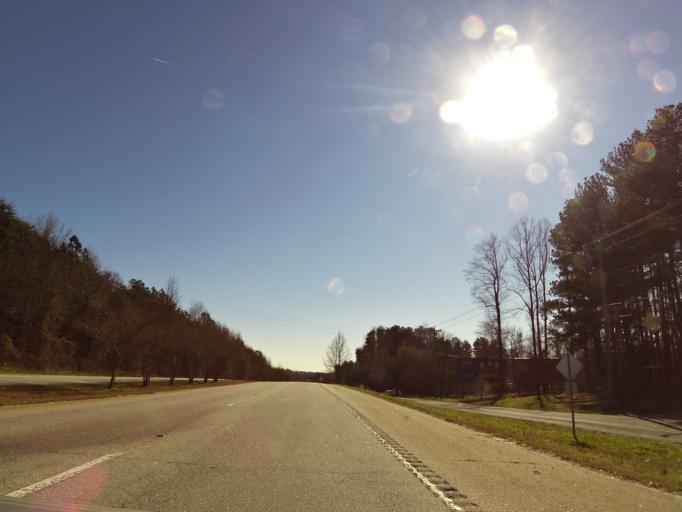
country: US
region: South Carolina
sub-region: Greenville County
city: Travelers Rest
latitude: 34.9424
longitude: -82.4358
